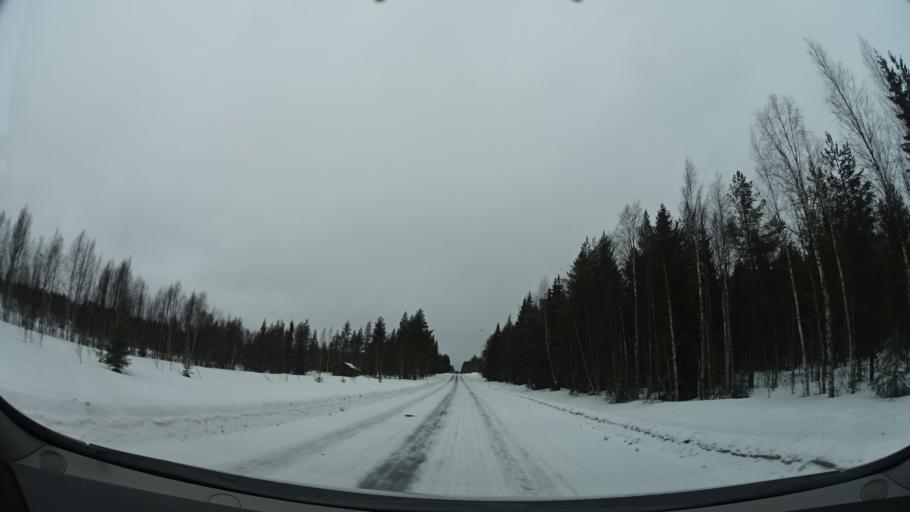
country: SE
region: Vaesterbotten
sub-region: Mala Kommun
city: Mala
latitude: 65.0920
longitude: 18.9444
